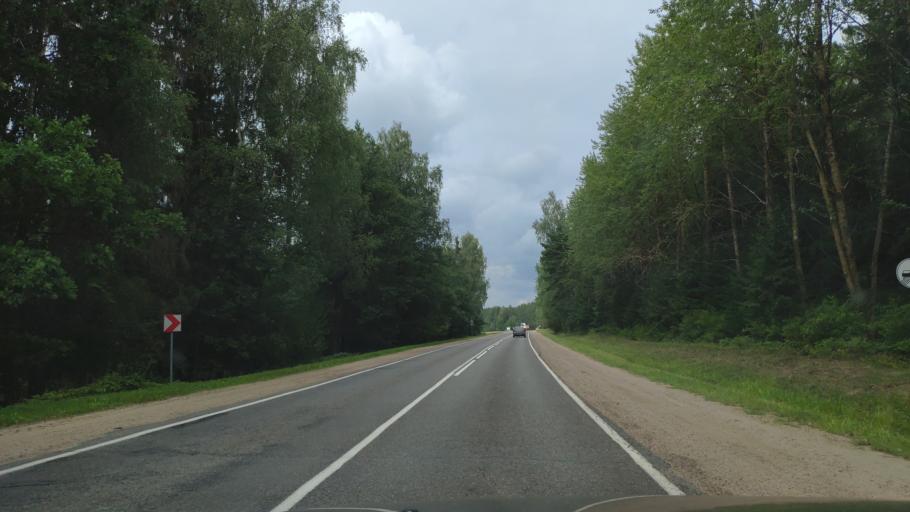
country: BY
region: Minsk
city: Zaslawye
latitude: 53.9660
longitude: 27.2449
